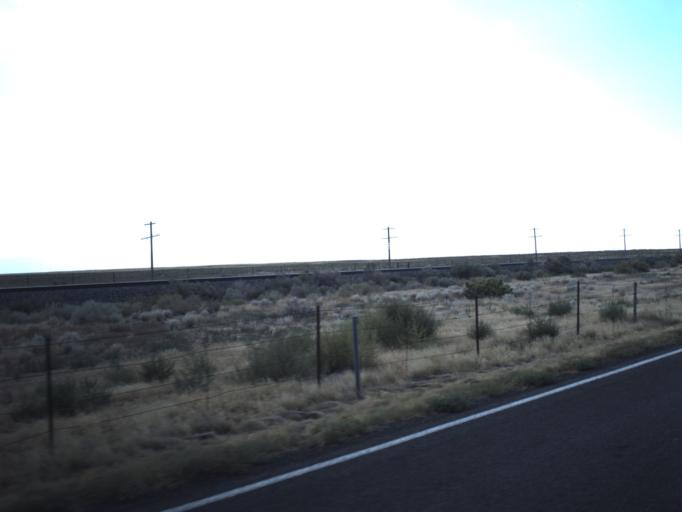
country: US
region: Utah
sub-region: Millard County
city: Delta
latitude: 38.9929
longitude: -112.7904
